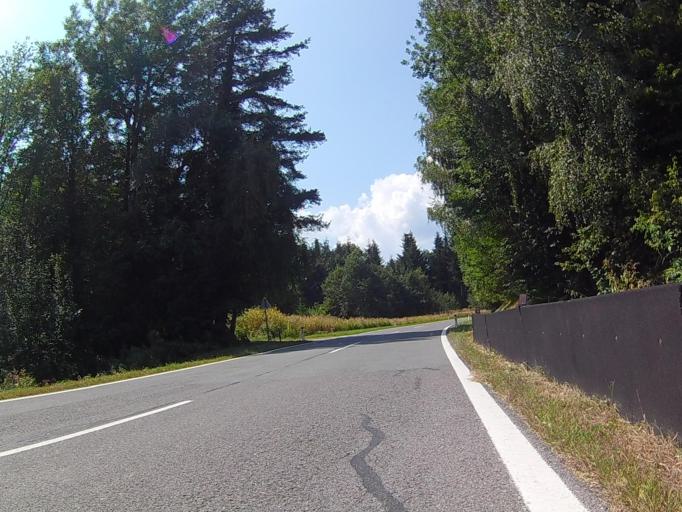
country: AT
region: Styria
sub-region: Politischer Bezirk Deutschlandsberg
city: Sankt Oswald ob Eibiswald
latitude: 46.7039
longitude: 15.1674
